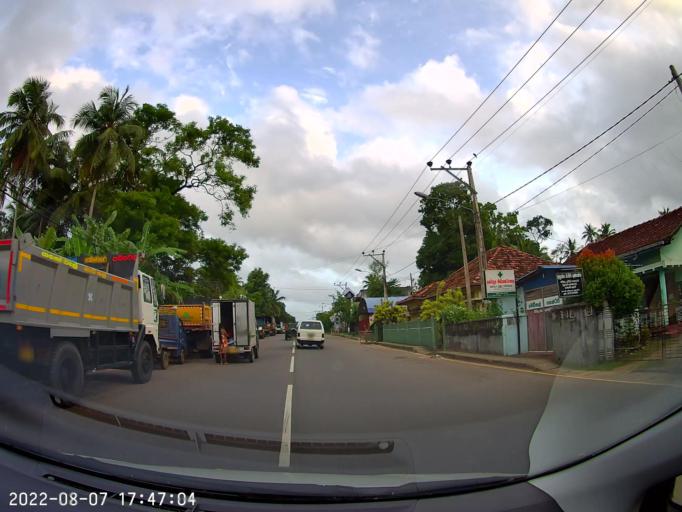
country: LK
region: North Western
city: Kuliyapitiya
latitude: 7.4680
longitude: 80.0265
